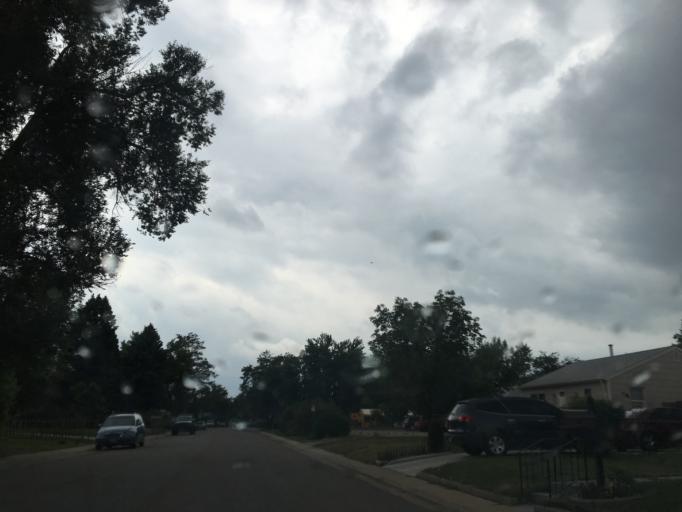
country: US
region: Colorado
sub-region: Arapahoe County
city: Sheridan
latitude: 39.6908
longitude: -105.0378
